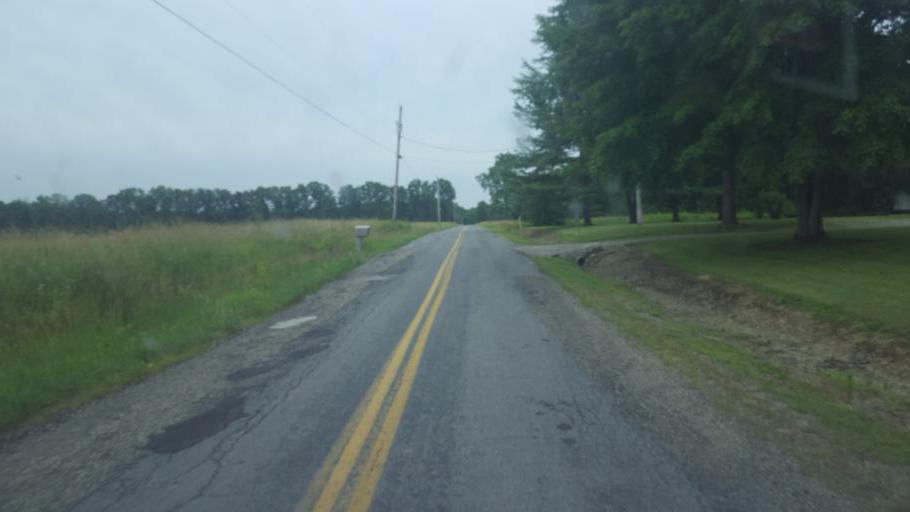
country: US
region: Ohio
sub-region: Trumbull County
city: South Canal
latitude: 41.1781
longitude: -81.0233
